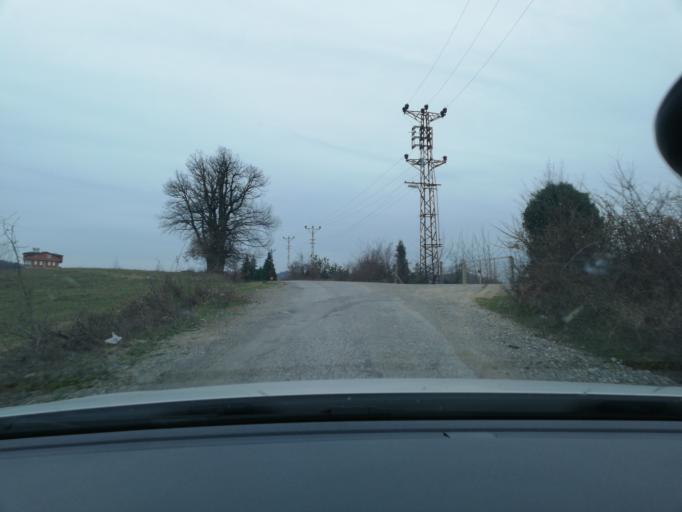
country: TR
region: Zonguldak
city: Gokcebey
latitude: 41.3138
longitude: 32.1362
